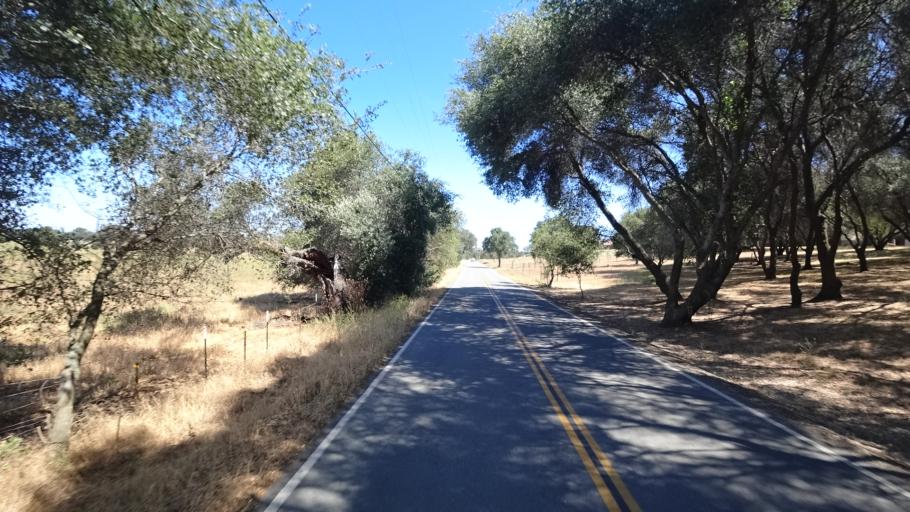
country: US
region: California
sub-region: Calaveras County
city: Rancho Calaveras
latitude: 38.1677
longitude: -120.9089
